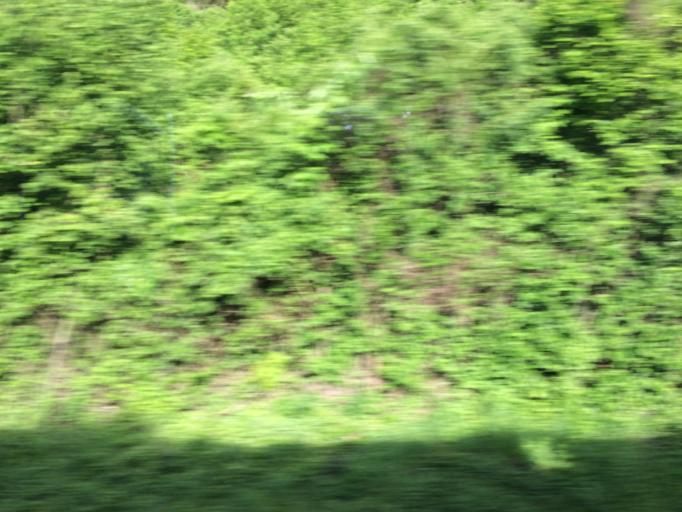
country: DE
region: Rheinland-Pfalz
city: Bacharach
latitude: 50.0695
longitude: 7.7781
